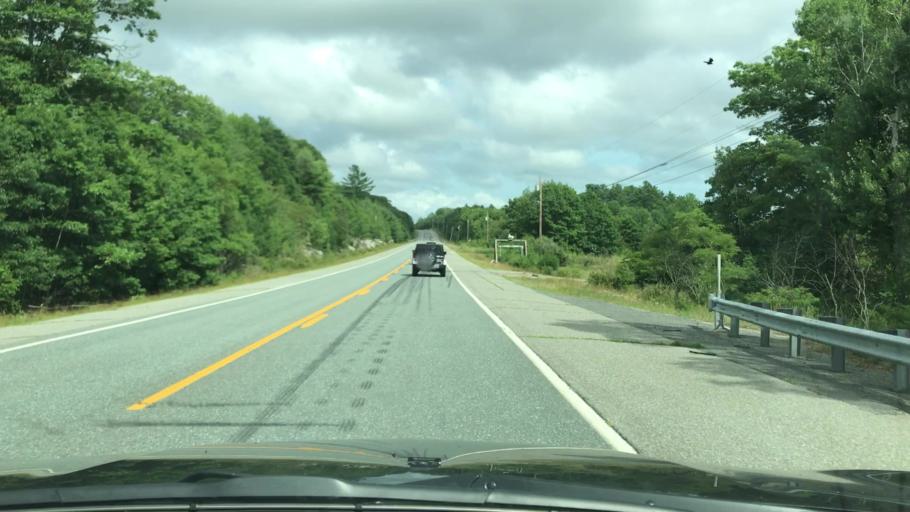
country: US
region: Maine
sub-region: Hancock County
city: Orland
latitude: 44.5659
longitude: -68.6109
